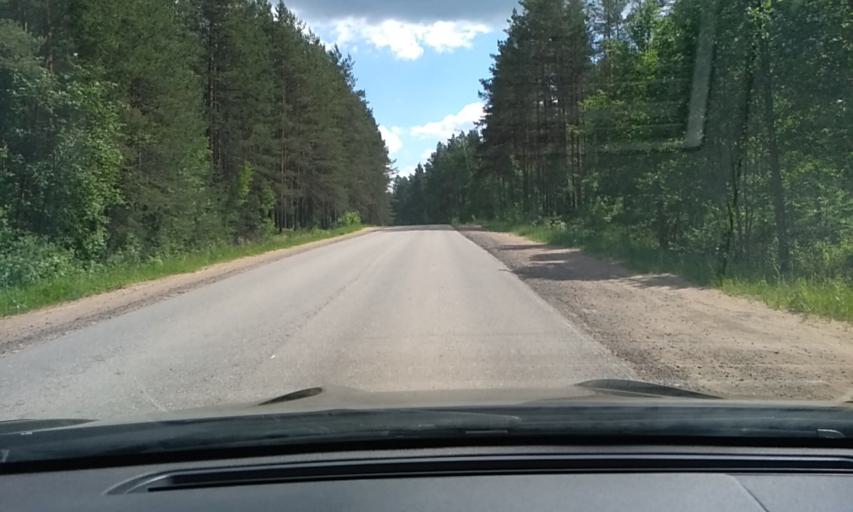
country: RU
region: Leningrad
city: Imeni Sverdlova
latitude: 59.8433
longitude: 30.6893
